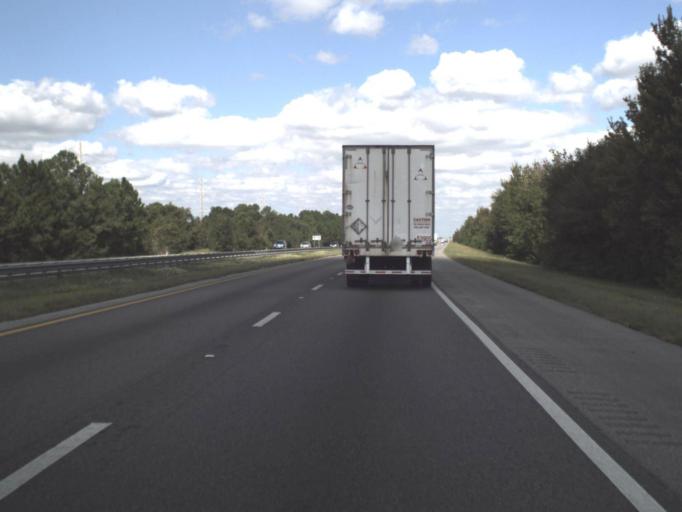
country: US
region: Florida
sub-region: Osceola County
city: Buenaventura Lakes
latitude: 28.3135
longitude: -81.3692
